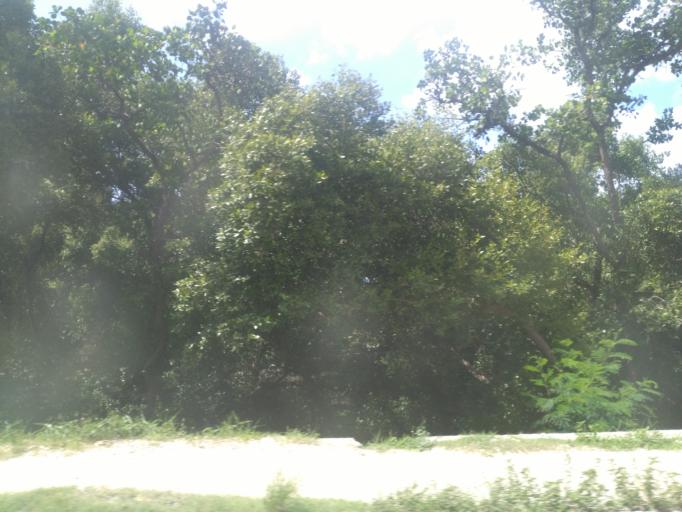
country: TZ
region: Zanzibar Urban/West
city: Zanzibar
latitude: -6.1583
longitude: 39.2022
